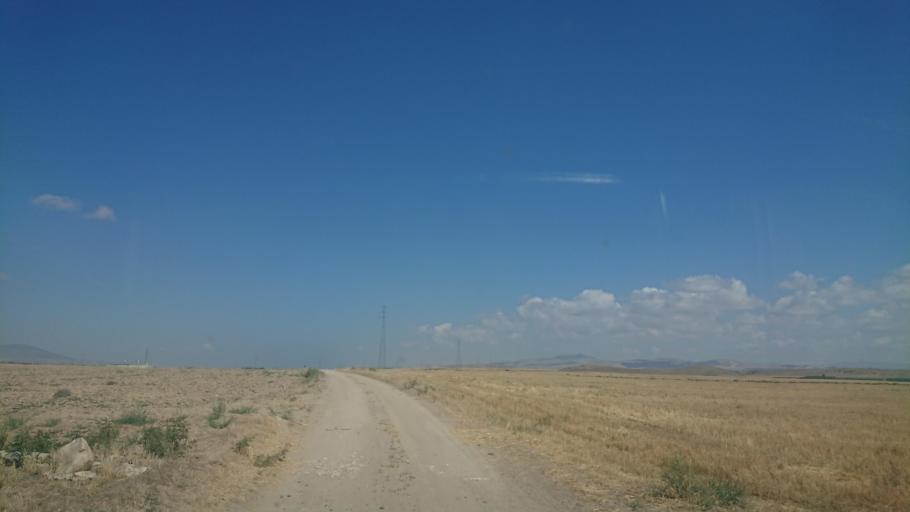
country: TR
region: Aksaray
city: Sariyahsi
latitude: 38.9997
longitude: 33.8919
